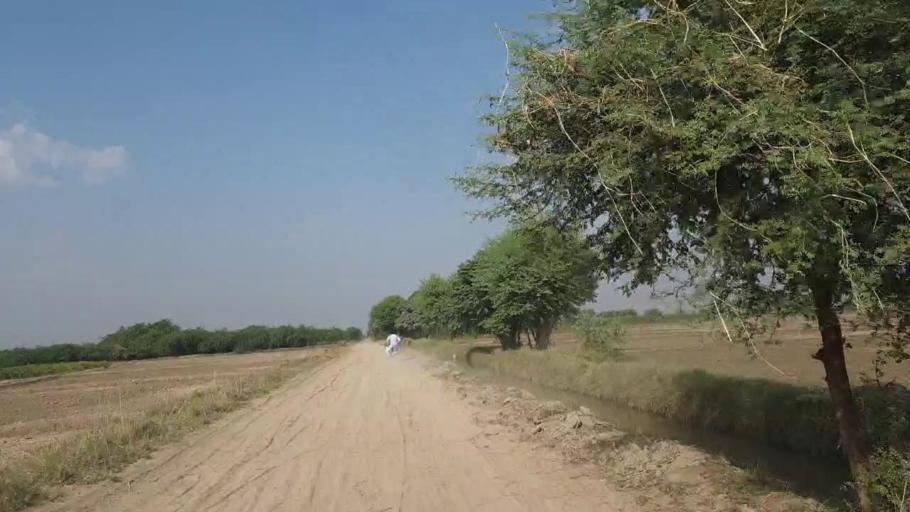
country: PK
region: Sindh
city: Digri
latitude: 25.0247
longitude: 69.0710
